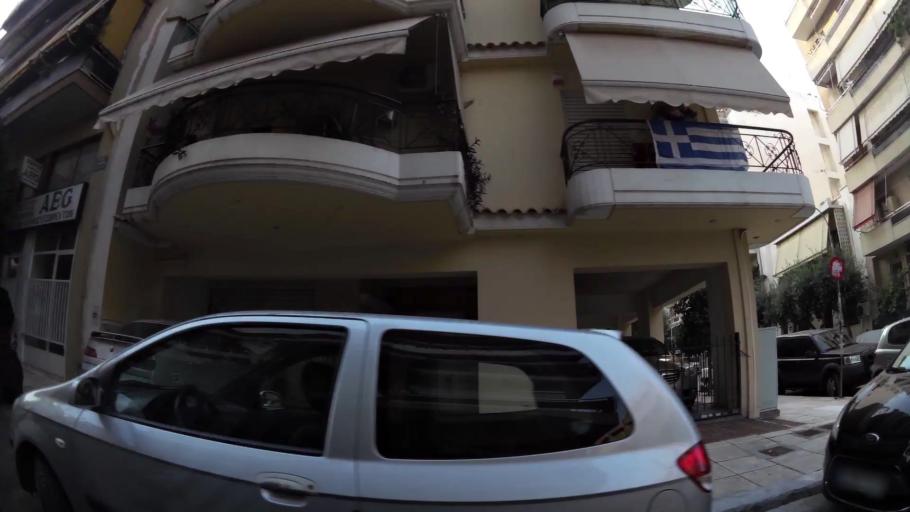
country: GR
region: Attica
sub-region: Nomarchia Athinas
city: Nea Smyrni
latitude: 37.9615
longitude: 23.7129
